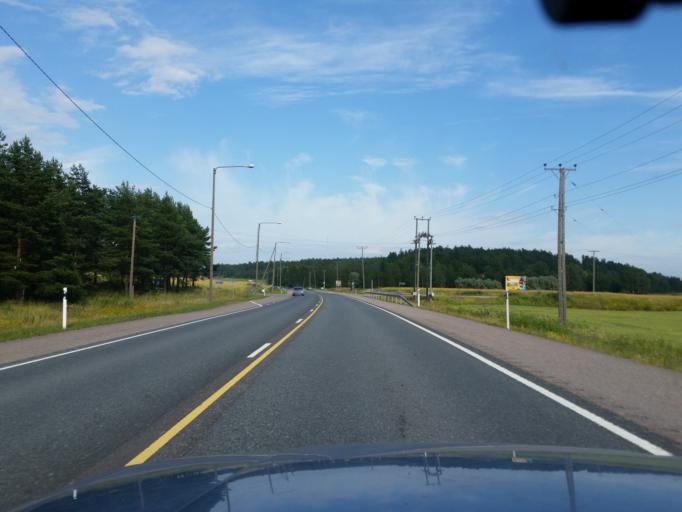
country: FI
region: Uusimaa
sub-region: Helsinki
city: Siuntio
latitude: 60.0812
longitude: 24.1732
